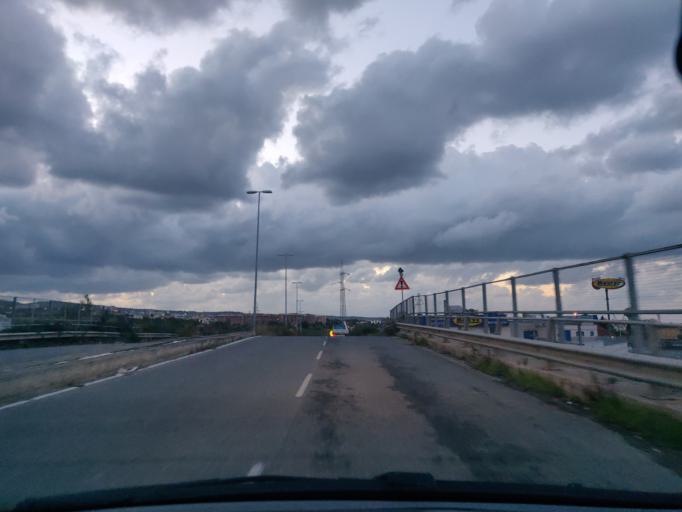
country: IT
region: Latium
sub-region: Citta metropolitana di Roma Capitale
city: Civitavecchia
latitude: 42.1085
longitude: 11.7864
